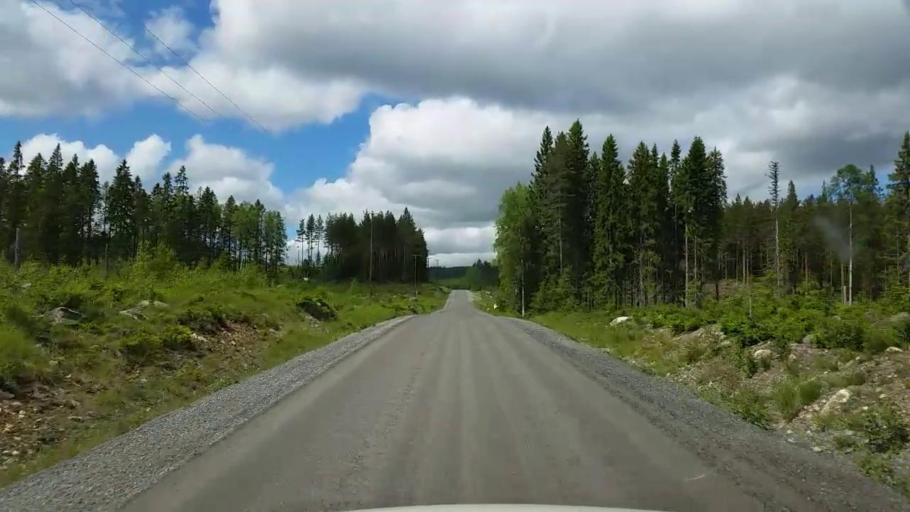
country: SE
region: Gaevleborg
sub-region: Bollnas Kommun
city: Vittsjo
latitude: 61.0870
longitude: 16.2509
